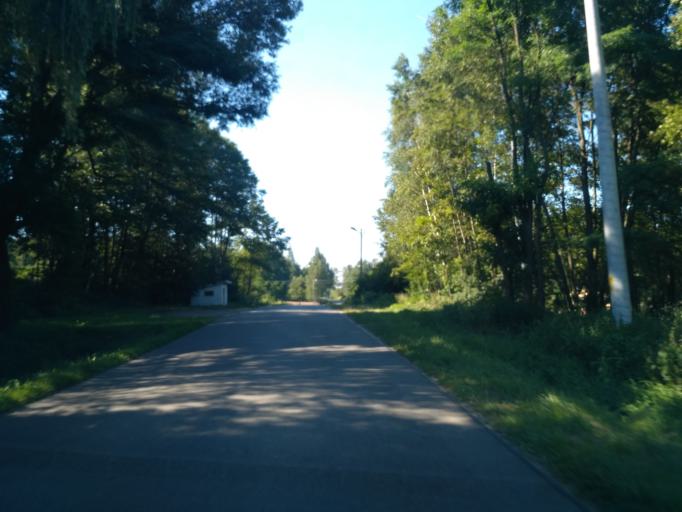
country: PL
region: Subcarpathian Voivodeship
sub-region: Powiat strzyzowski
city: Wysoka Strzyzowska
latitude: 49.7908
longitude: 21.7567
